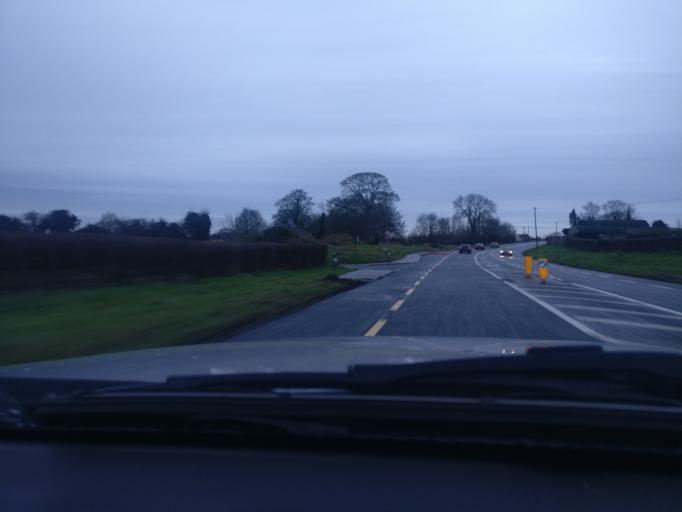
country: IE
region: Leinster
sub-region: An Mhi
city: Kells
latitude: 53.6928
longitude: -6.7832
